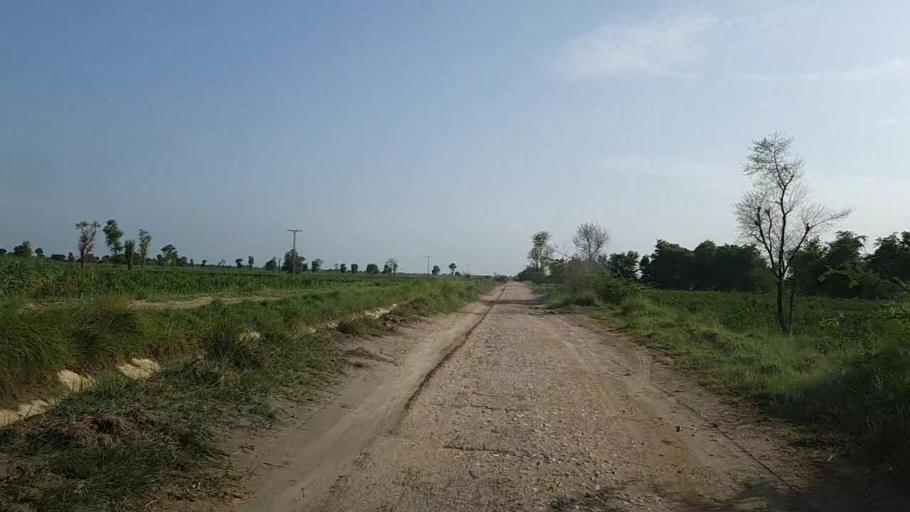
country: PK
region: Sindh
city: Pad Idan
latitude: 26.8325
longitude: 68.2425
